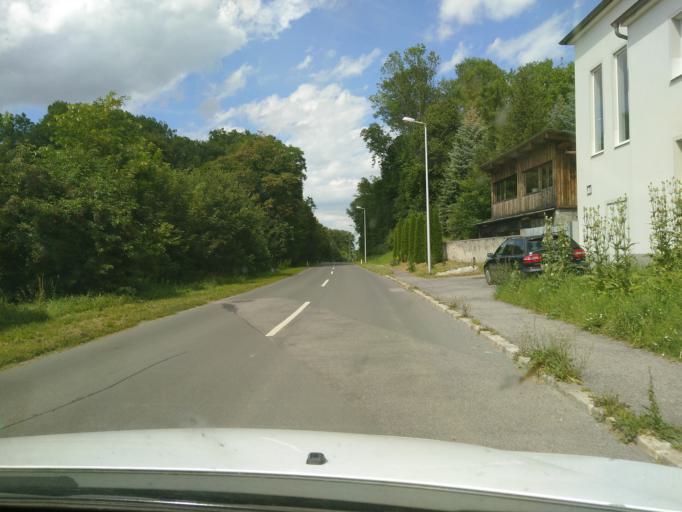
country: AT
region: Burgenland
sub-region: Politischer Bezirk Oberpullendorf
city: Nikitsch
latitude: 47.5302
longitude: 16.6483
